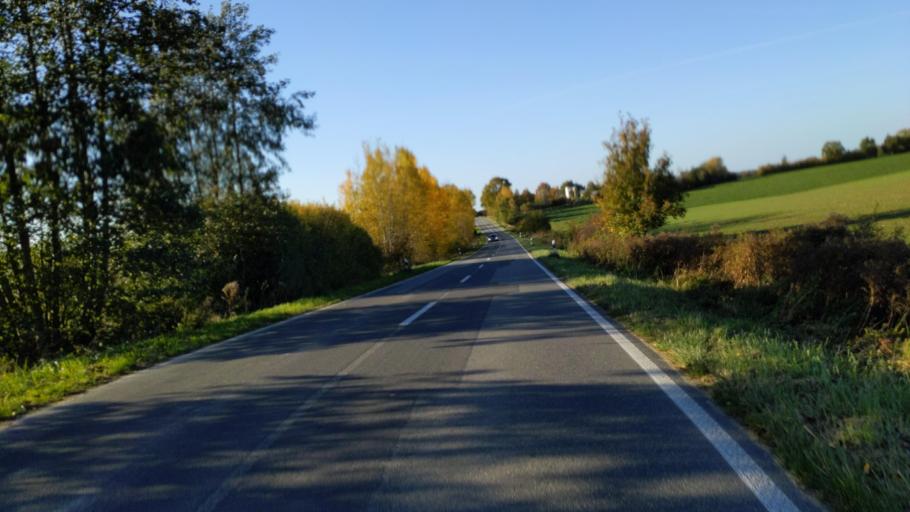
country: DE
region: Schleswig-Holstein
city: Gross Sarau
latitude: 53.7724
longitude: 10.7218
